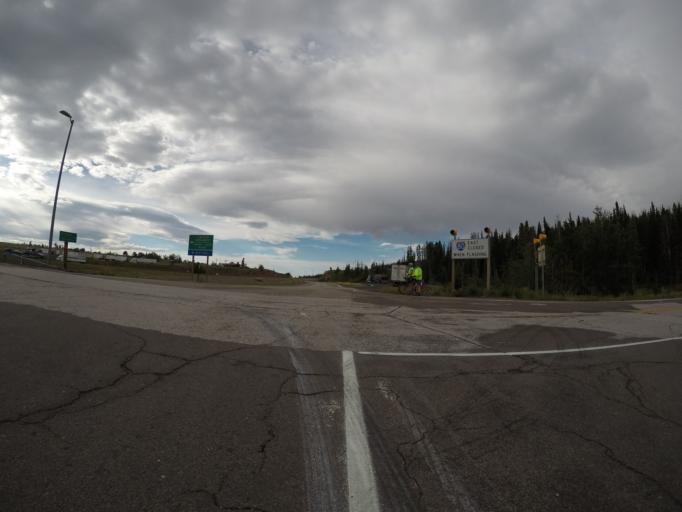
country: US
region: Wyoming
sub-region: Albany County
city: Laramie
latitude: 41.2399
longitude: -105.4389
